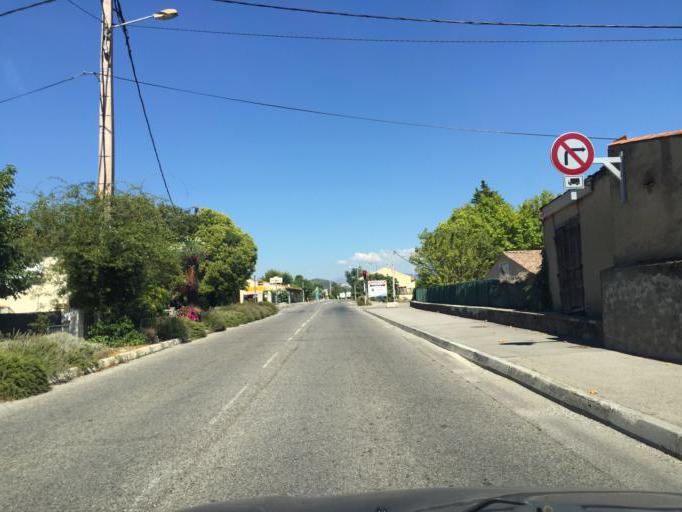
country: FR
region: Provence-Alpes-Cote d'Azur
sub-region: Departement des Alpes-de-Haute-Provence
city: Peyruis
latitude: 44.0289
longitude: 5.9411
